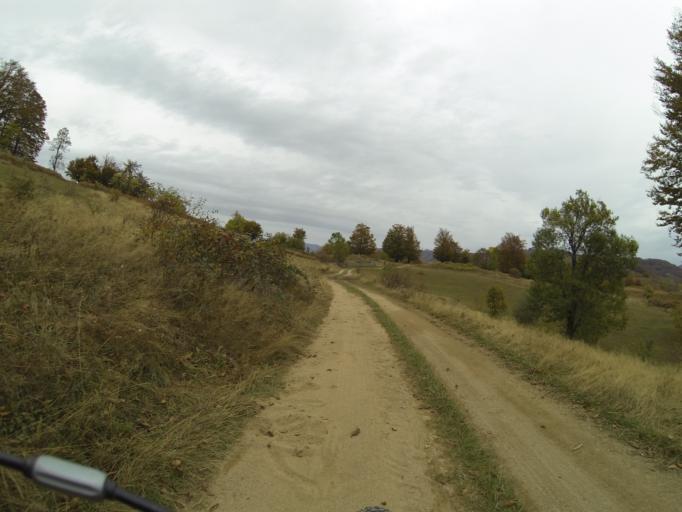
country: RO
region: Gorj
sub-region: Comuna Pades
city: Closani
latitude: 45.1179
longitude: 22.8506
